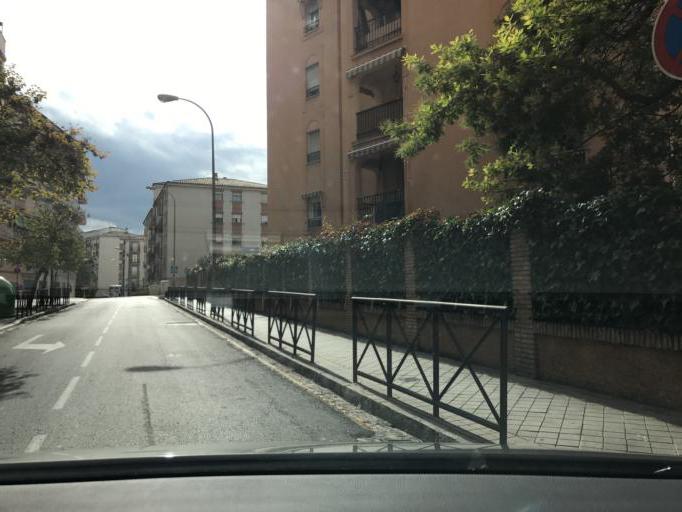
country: ES
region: Andalusia
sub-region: Provincia de Granada
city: Granada
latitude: 37.1659
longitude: -3.6007
